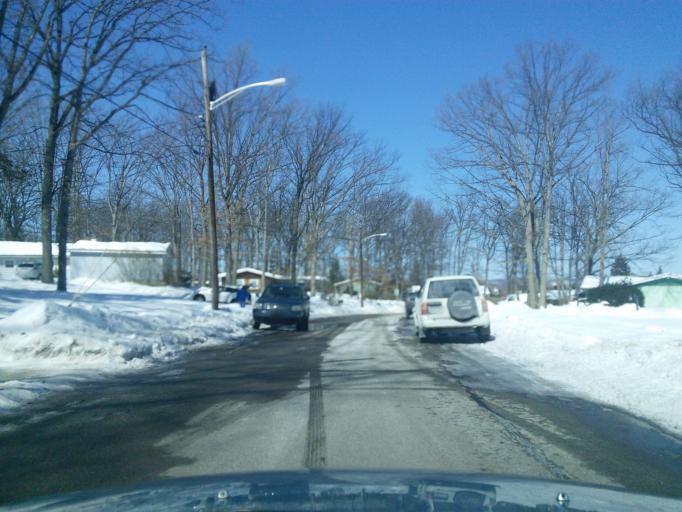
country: US
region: Pennsylvania
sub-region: Centre County
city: Park Forest Village
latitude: 40.8071
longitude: -77.9071
